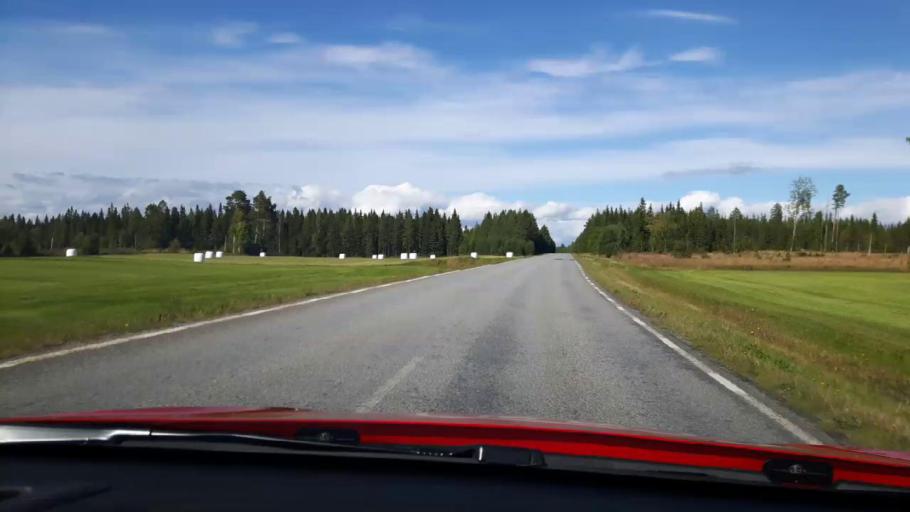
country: SE
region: Jaemtland
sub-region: OEstersunds Kommun
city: Ostersund
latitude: 63.0637
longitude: 14.4473
